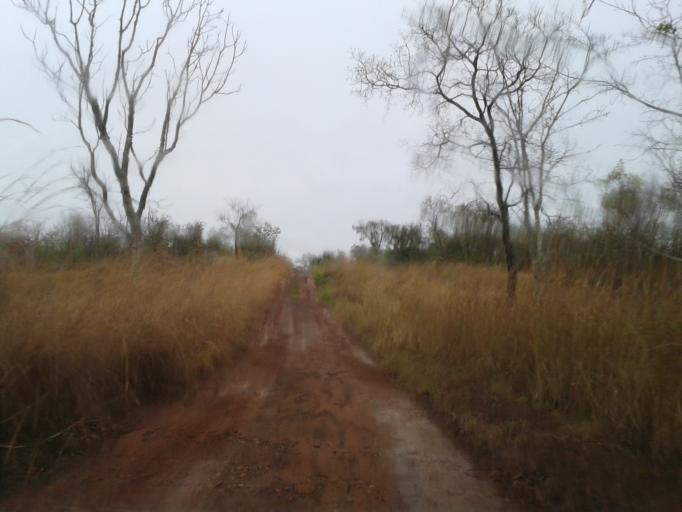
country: BR
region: Minas Gerais
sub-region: Campina Verde
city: Campina Verde
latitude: -19.3309
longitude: -49.5164
